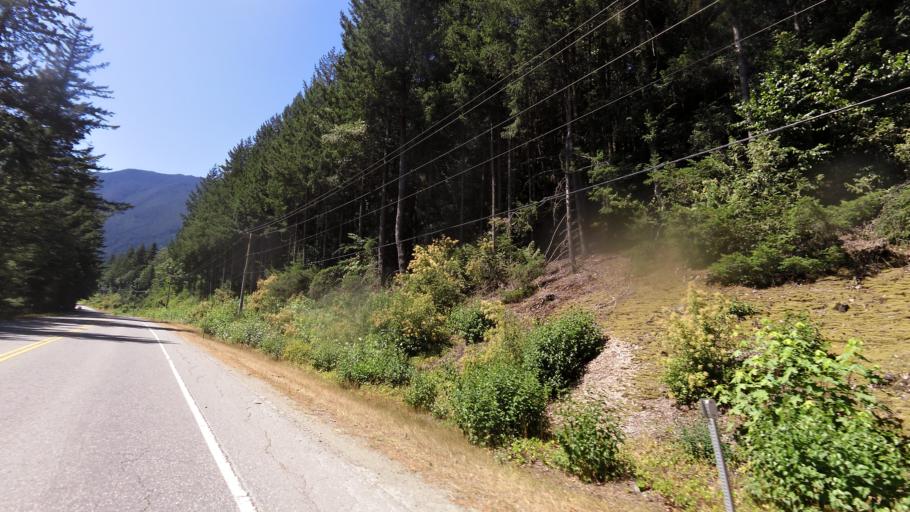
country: CA
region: British Columbia
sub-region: Fraser Valley Regional District
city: Chilliwack
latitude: 49.2445
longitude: -121.9859
